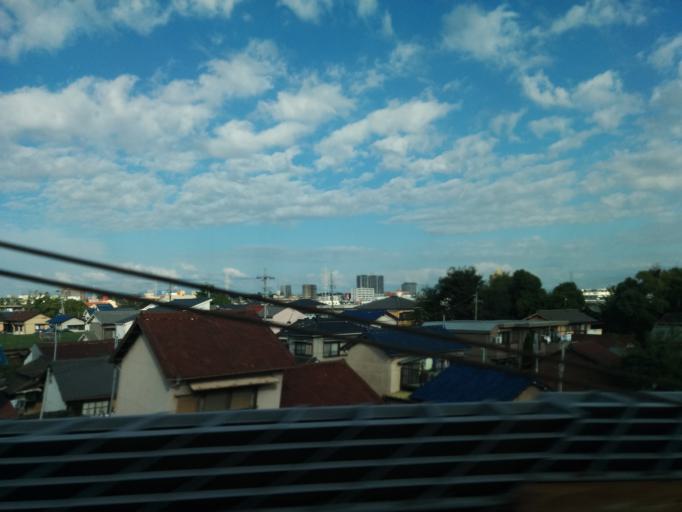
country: JP
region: Aichi
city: Obu
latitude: 35.0766
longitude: 136.9366
